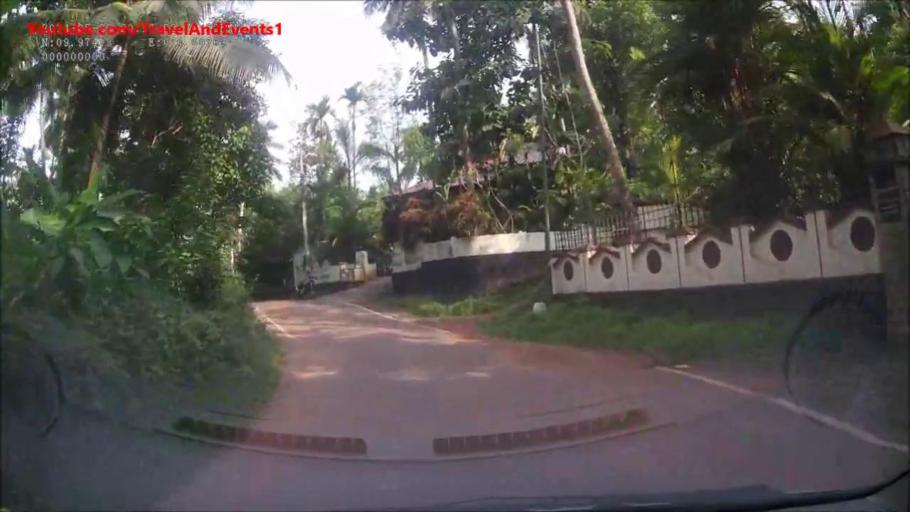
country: IN
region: Kerala
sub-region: Ernakulam
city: Muvattupula
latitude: 9.9677
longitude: 76.6110
